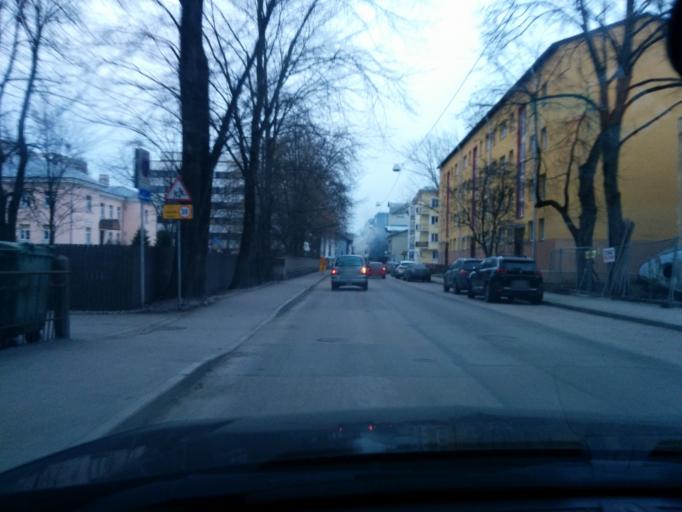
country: EE
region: Harju
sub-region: Tallinna linn
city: Tallinn
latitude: 59.4370
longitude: 24.7709
